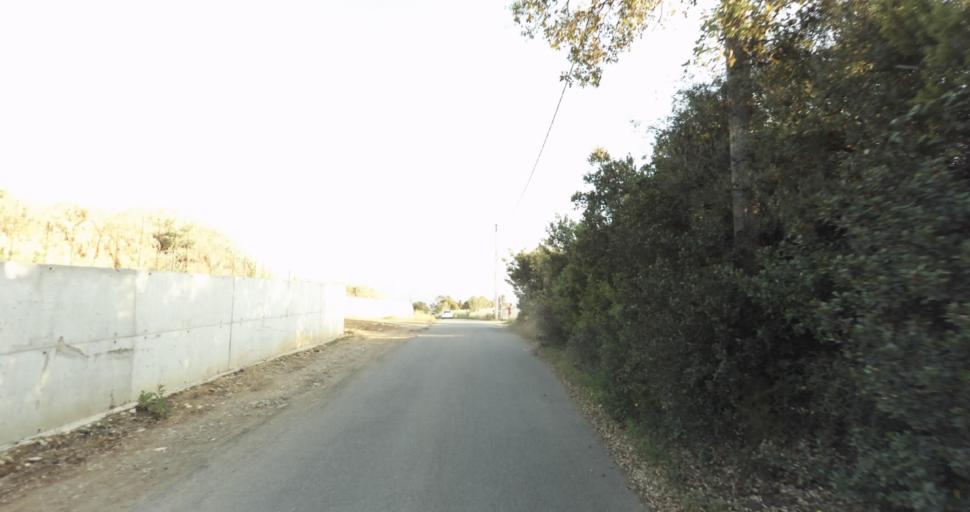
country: FR
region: Corsica
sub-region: Departement de la Haute-Corse
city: Biguglia
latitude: 42.6030
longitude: 9.4453
